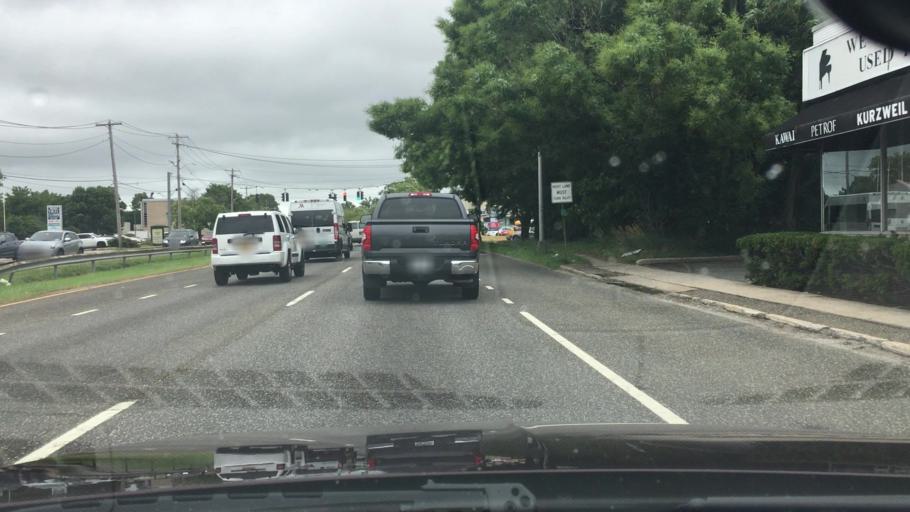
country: US
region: New York
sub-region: Suffolk County
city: South Huntington
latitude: 40.8138
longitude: -73.4099
